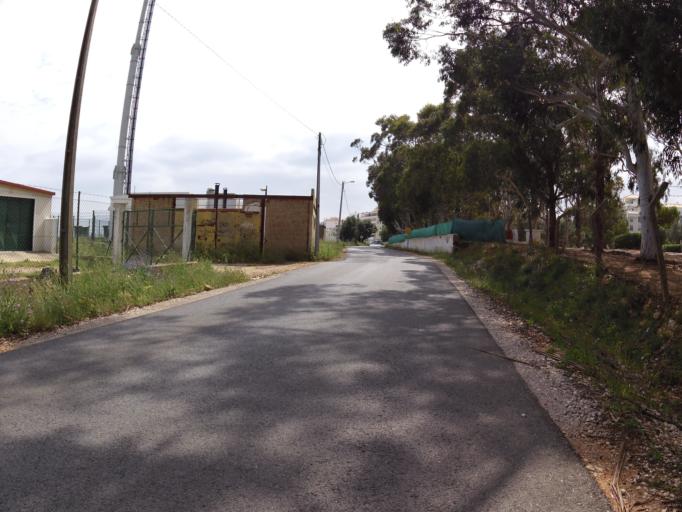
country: PT
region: Faro
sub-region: Silves
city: Armacao de Pera
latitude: 37.1074
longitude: -8.3513
